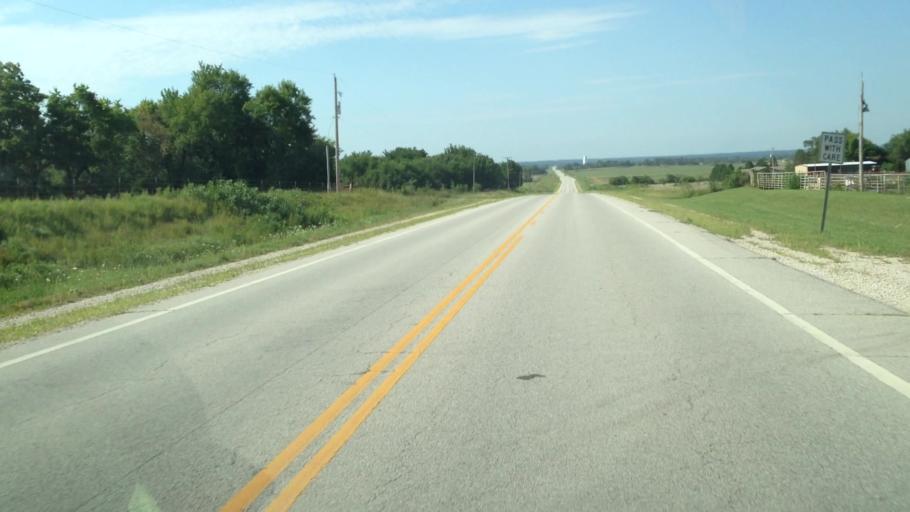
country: US
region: Kansas
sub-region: Neosho County
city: Erie
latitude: 37.4776
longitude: -95.2692
